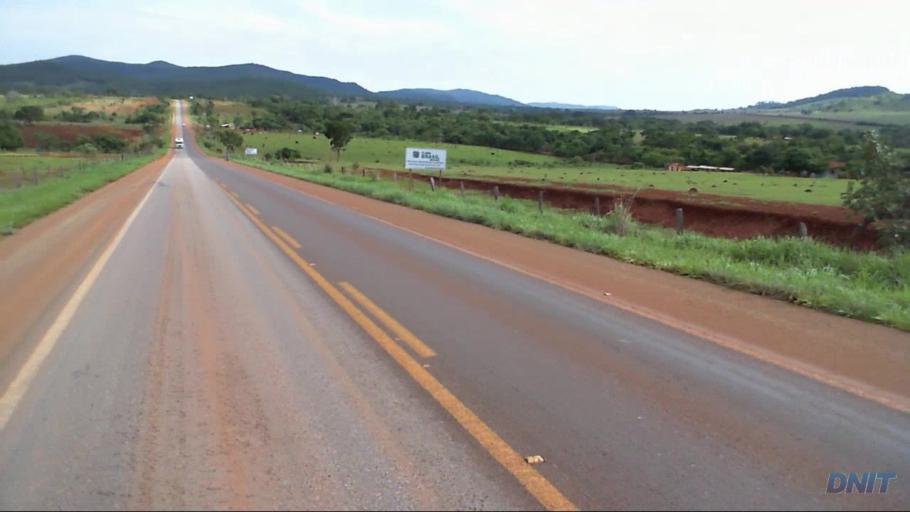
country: BR
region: Goias
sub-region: Barro Alto
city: Barro Alto
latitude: -14.9608
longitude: -48.9315
